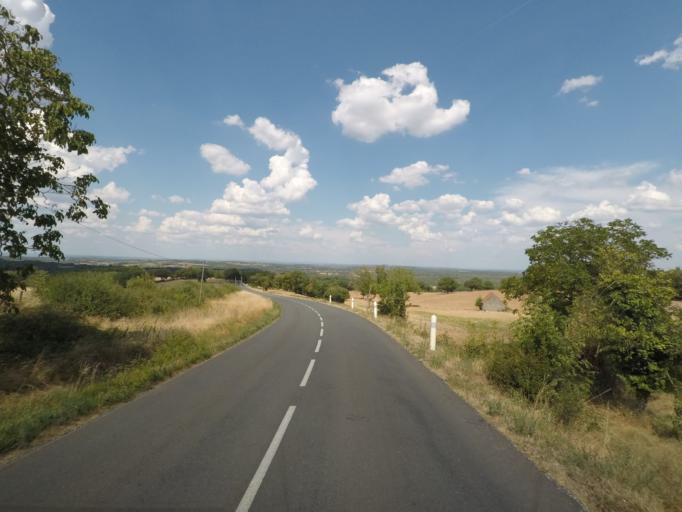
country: FR
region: Midi-Pyrenees
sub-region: Departement du Lot
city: Le Vigan
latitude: 44.6637
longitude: 1.5907
